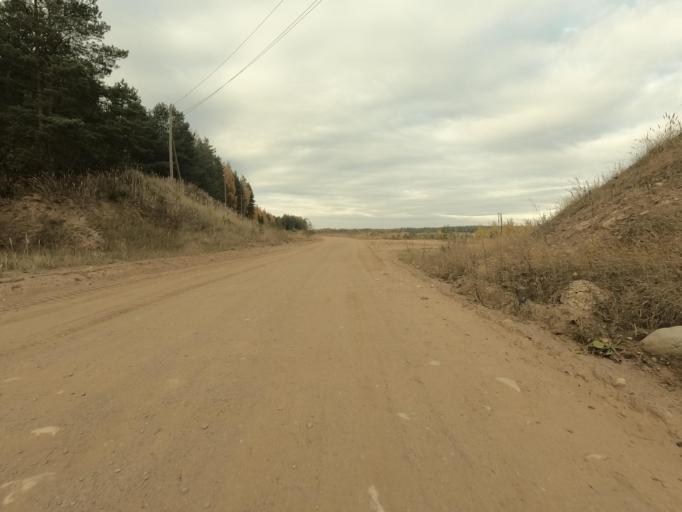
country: RU
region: Leningrad
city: Priladozhskiy
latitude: 59.7000
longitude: 31.3625
